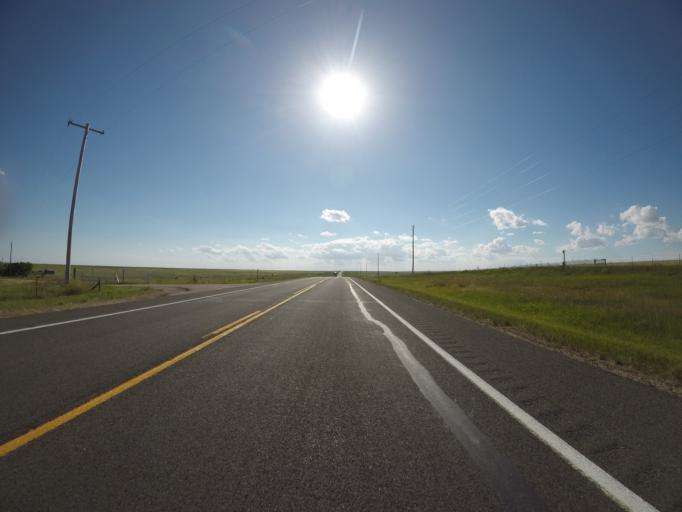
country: US
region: Colorado
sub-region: Morgan County
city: Brush
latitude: 40.6099
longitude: -103.7095
